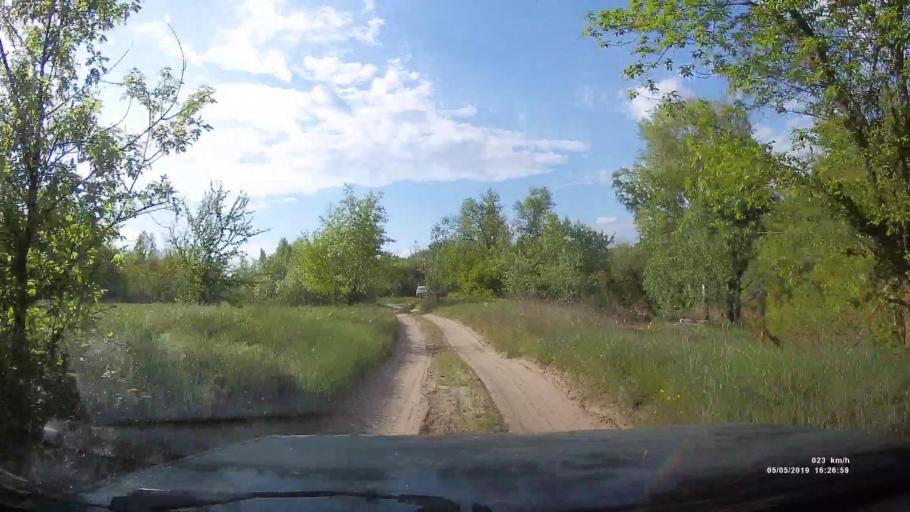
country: RU
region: Rostov
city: Ust'-Donetskiy
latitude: 47.7641
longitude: 41.0204
